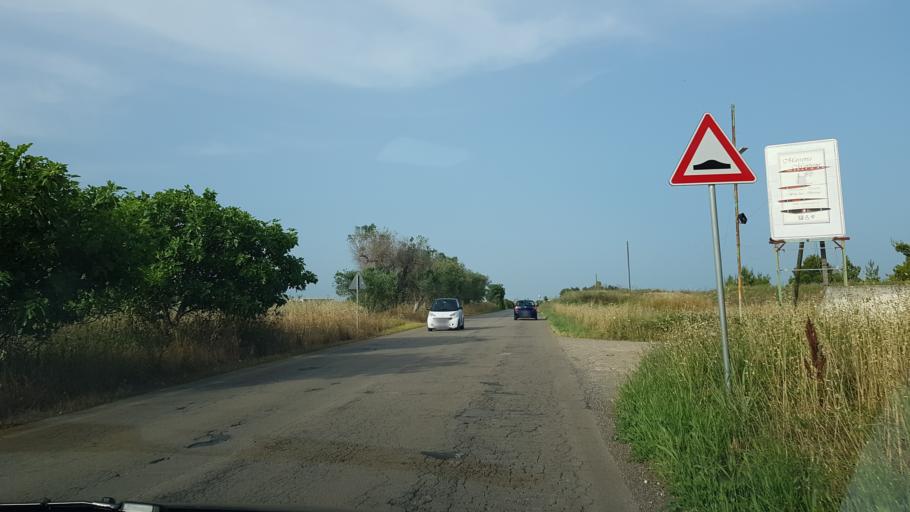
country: IT
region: Apulia
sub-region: Provincia di Brindisi
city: San Donaci
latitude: 40.4363
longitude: 17.8913
